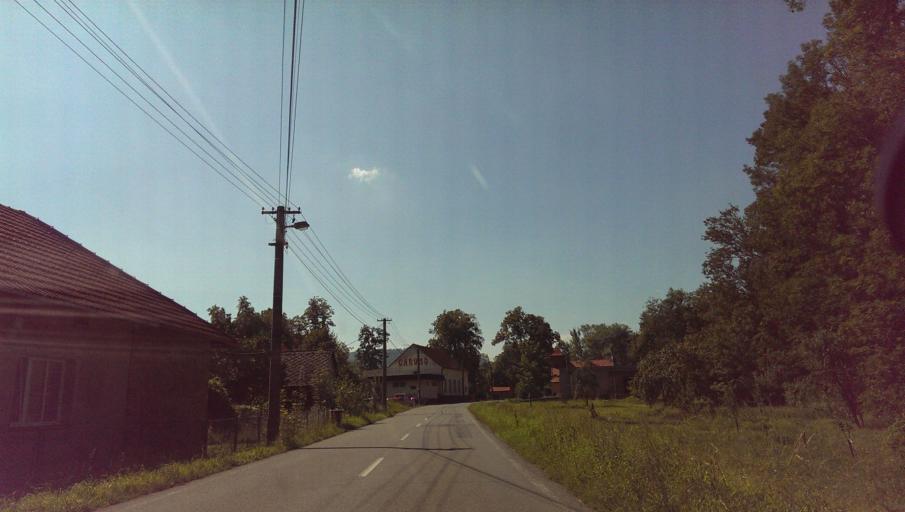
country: CZ
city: Hukvaldy
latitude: 49.6454
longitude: 18.2188
